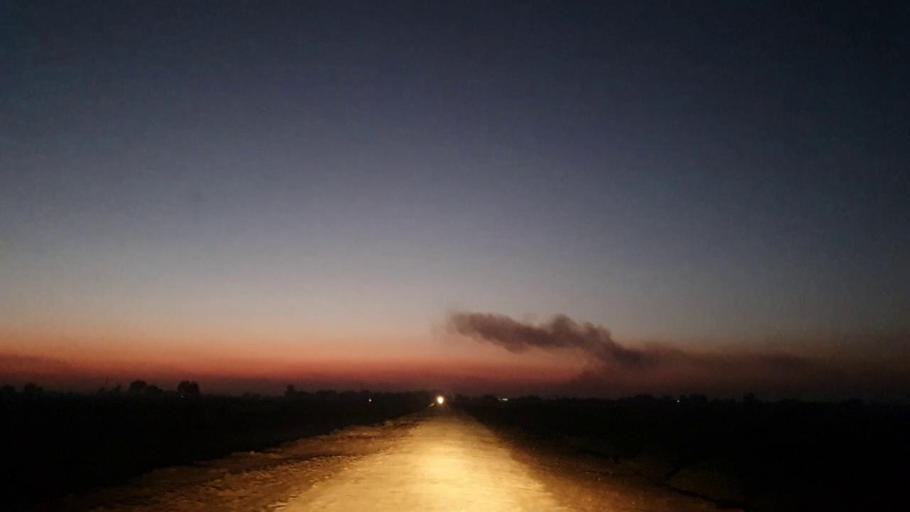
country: PK
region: Sindh
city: Nawabshah
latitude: 26.3185
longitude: 68.3705
